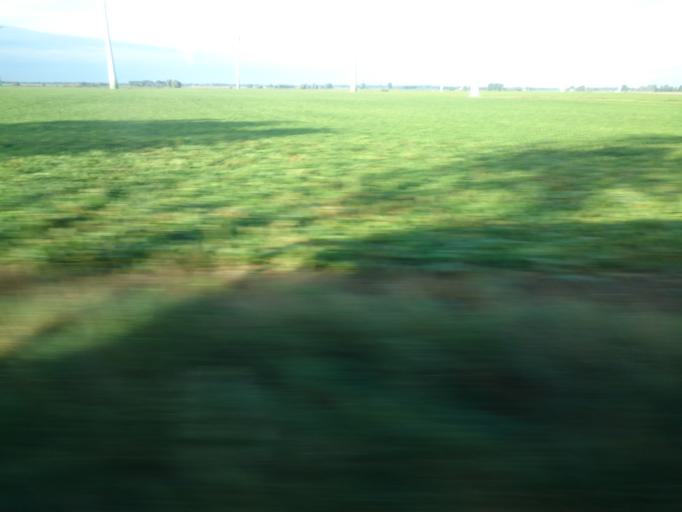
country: DE
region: Mecklenburg-Vorpommern
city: Anklam
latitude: 53.9193
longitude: 13.6457
